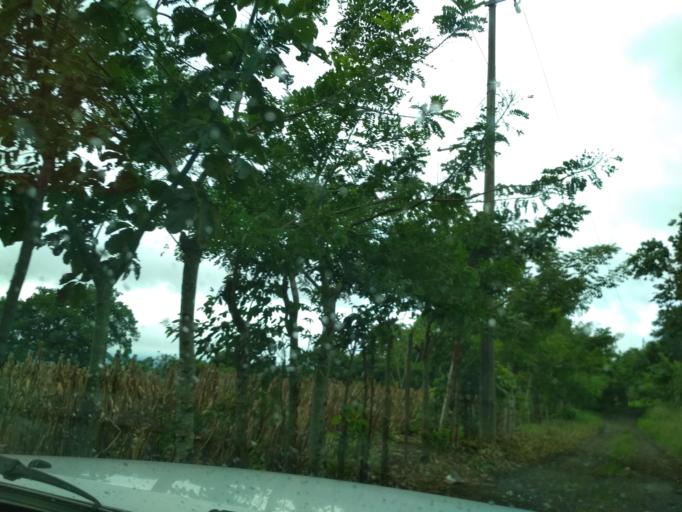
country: MX
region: Veracruz
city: Santiago Tuxtla
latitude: 18.4356
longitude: -95.3023
